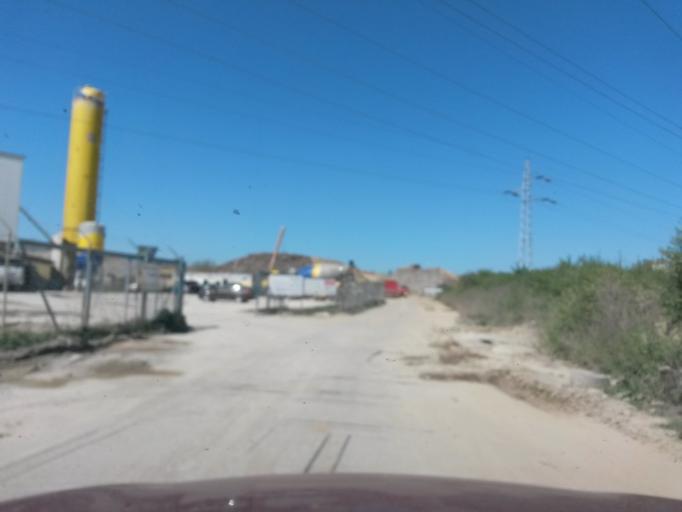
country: SK
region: Kosicky
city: Kosice
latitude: 48.6742
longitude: 21.2762
